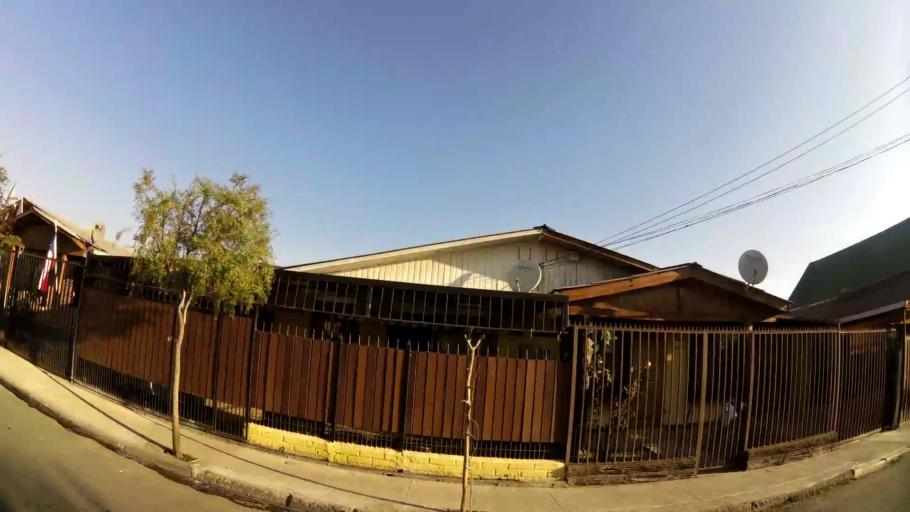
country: CL
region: Santiago Metropolitan
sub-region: Provincia de Santiago
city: La Pintana
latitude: -33.5489
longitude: -70.6236
